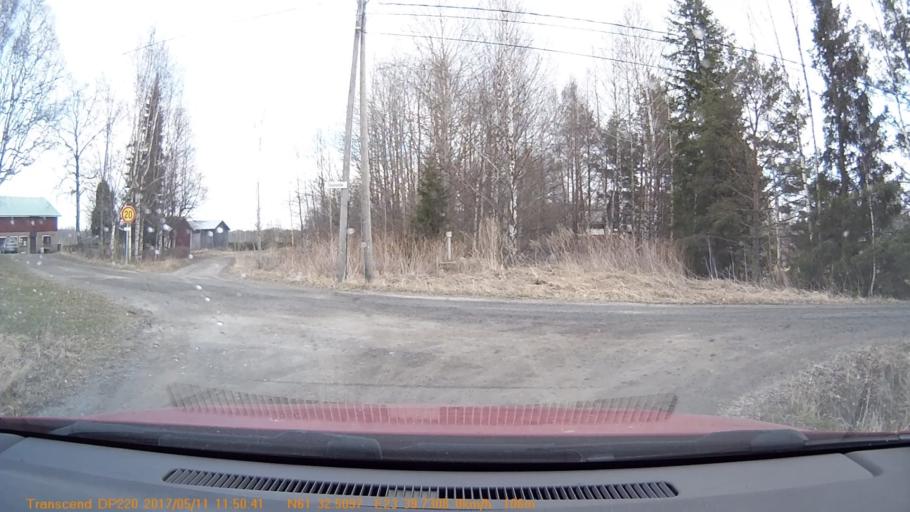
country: FI
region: Pirkanmaa
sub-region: Tampere
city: Yloejaervi
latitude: 61.5418
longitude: 23.6622
